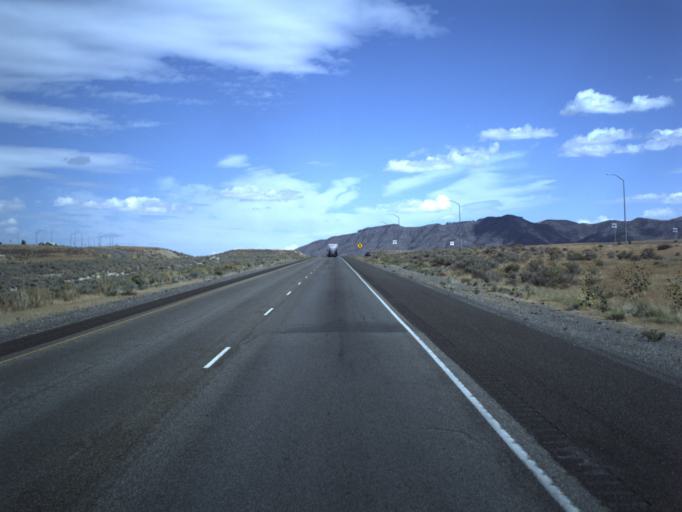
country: US
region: Utah
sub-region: Tooele County
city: Grantsville
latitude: 40.7578
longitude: -113.0180
